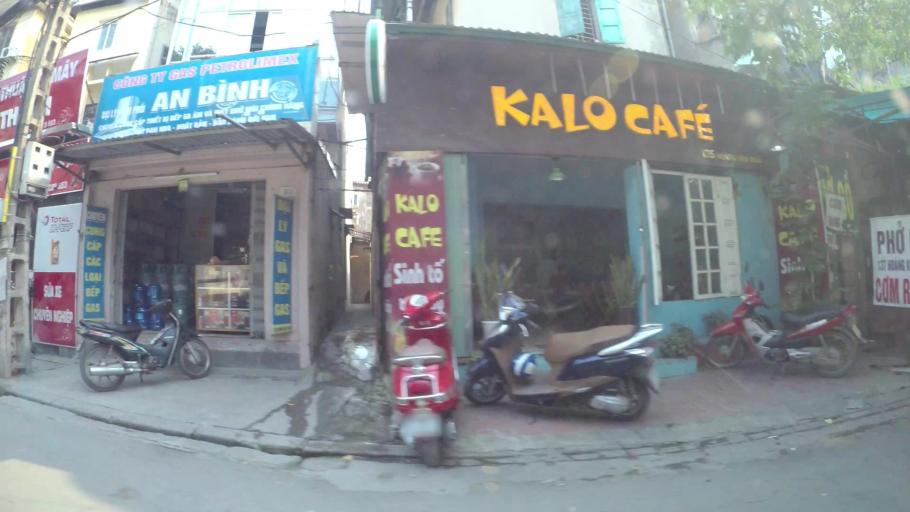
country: VN
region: Ha Noi
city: Dong Da
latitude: 20.9972
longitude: 105.8239
